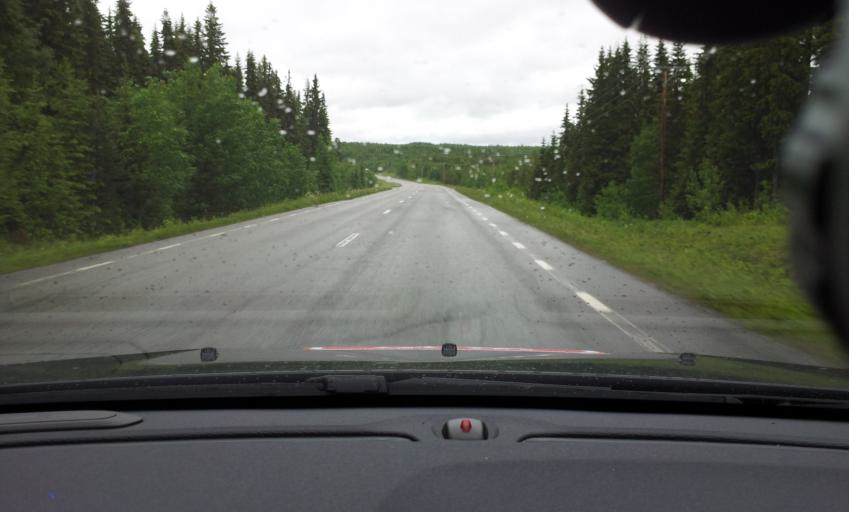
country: SE
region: Jaemtland
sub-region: Krokoms Kommun
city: Krokom
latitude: 63.5385
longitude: 14.5774
